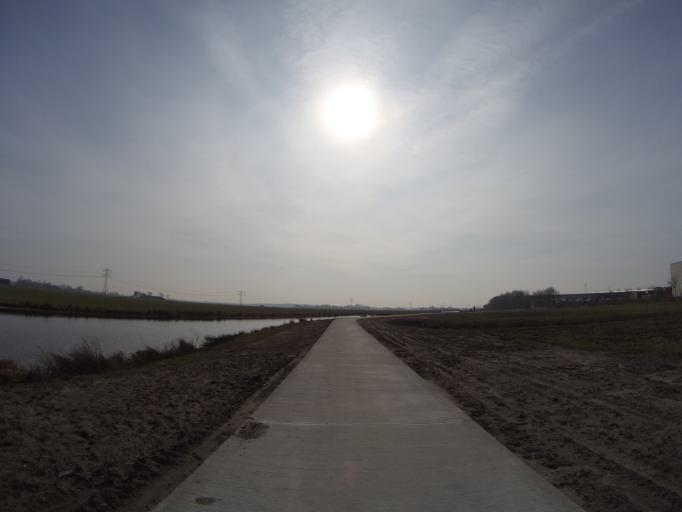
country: NL
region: Utrecht
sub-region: Gemeente Bunschoten
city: Bunschoten
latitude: 52.2307
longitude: 5.3831
